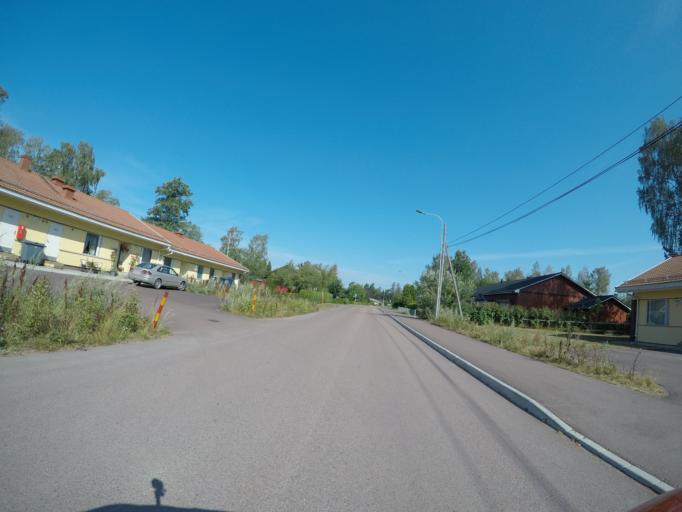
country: AX
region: Alands landsbygd
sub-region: Finstroem
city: Finstroem
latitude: 60.2262
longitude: 19.9796
